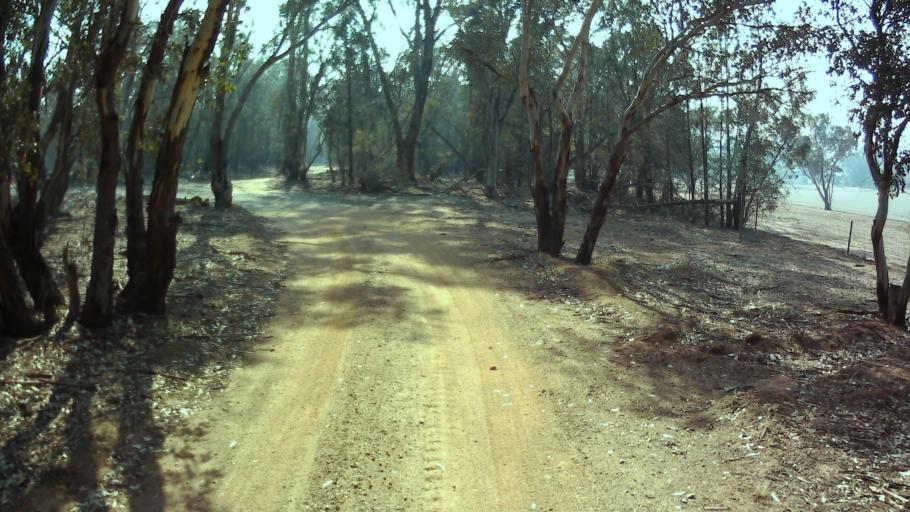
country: AU
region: New South Wales
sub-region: Weddin
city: Grenfell
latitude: -33.8961
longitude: 148.1807
